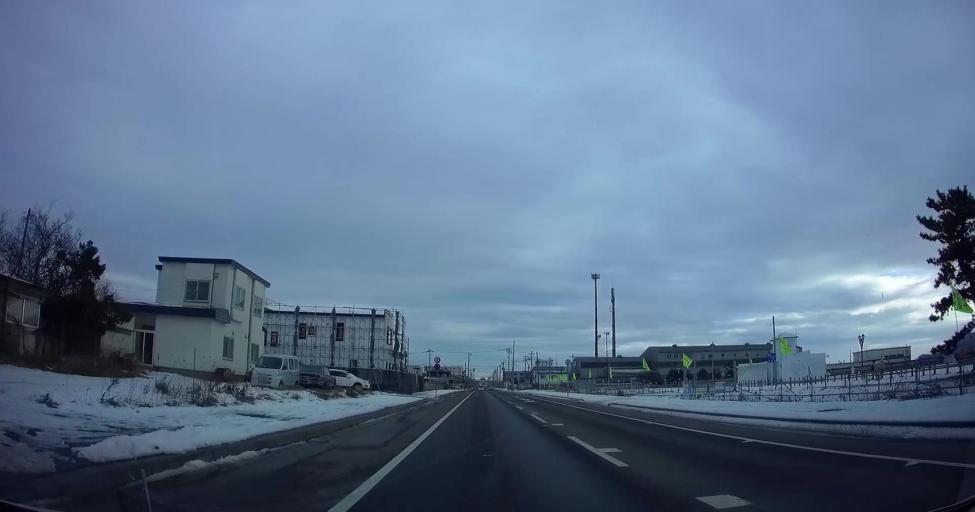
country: JP
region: Hokkaido
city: Hakodate
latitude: 41.8146
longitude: 140.7038
